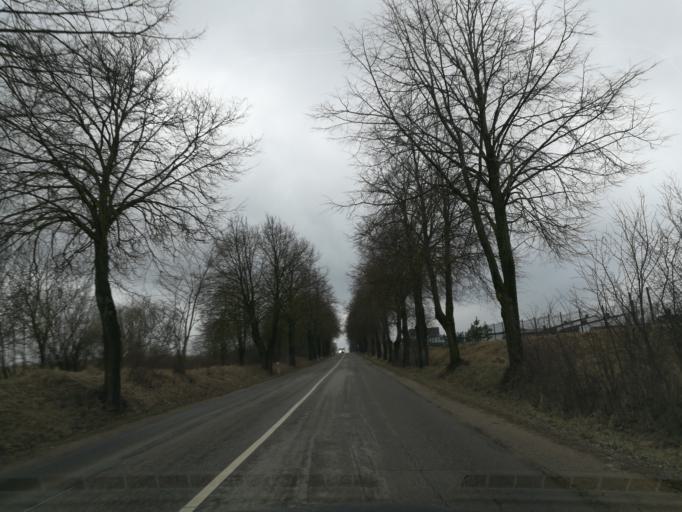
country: LT
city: Lentvaris
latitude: 54.6434
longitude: 25.0891
